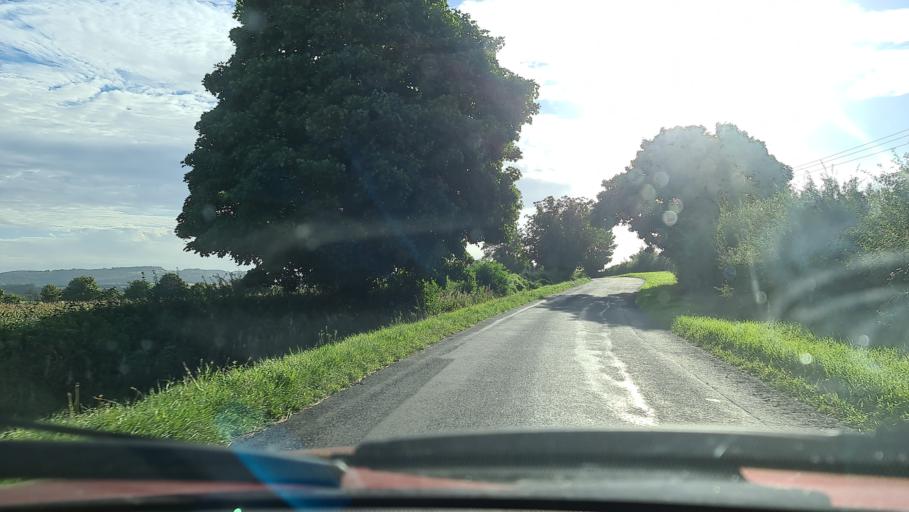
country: GB
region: England
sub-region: Buckinghamshire
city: Princes Risborough
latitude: 51.7038
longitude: -0.8630
